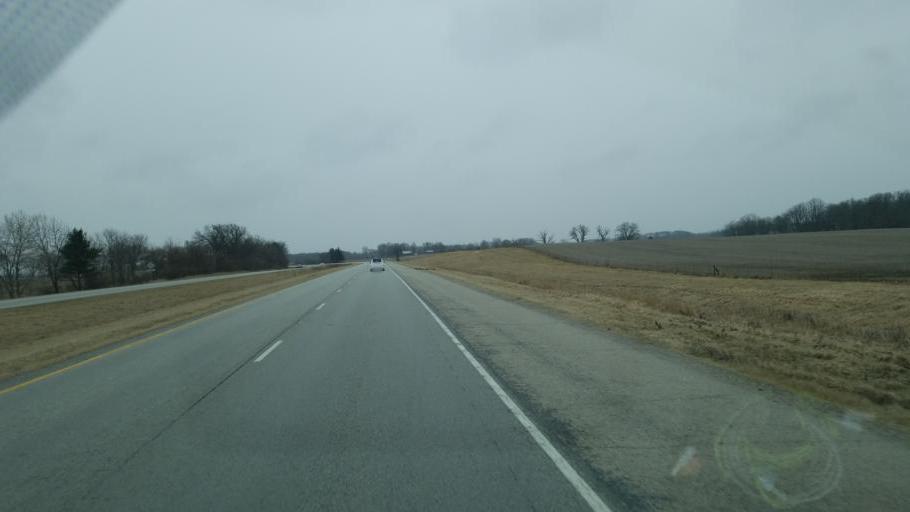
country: US
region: Indiana
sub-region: Fulton County
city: Rochester
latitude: 40.9066
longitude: -86.1595
